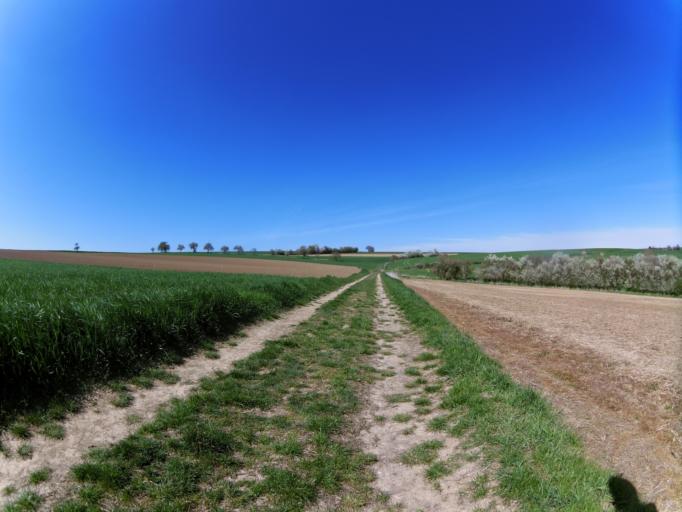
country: DE
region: Bavaria
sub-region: Regierungsbezirk Unterfranken
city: Winterhausen
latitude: 49.6777
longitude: 9.9995
